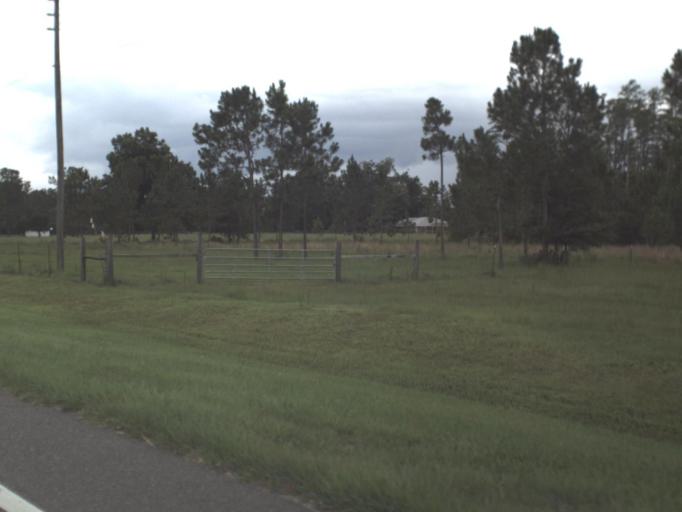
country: US
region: Florida
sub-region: Clay County
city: Keystone Heights
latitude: 29.8613
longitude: -82.0736
